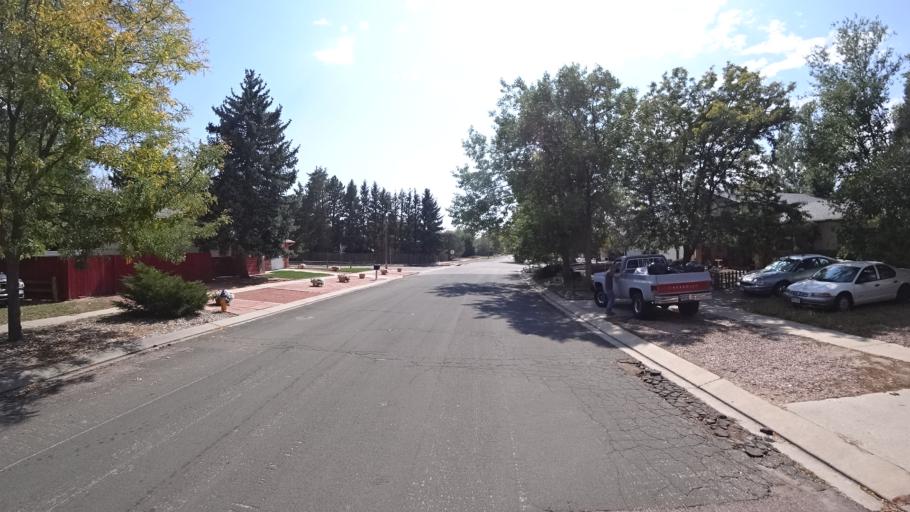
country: US
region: Colorado
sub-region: El Paso County
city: Colorado Springs
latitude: 38.8517
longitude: -104.7625
